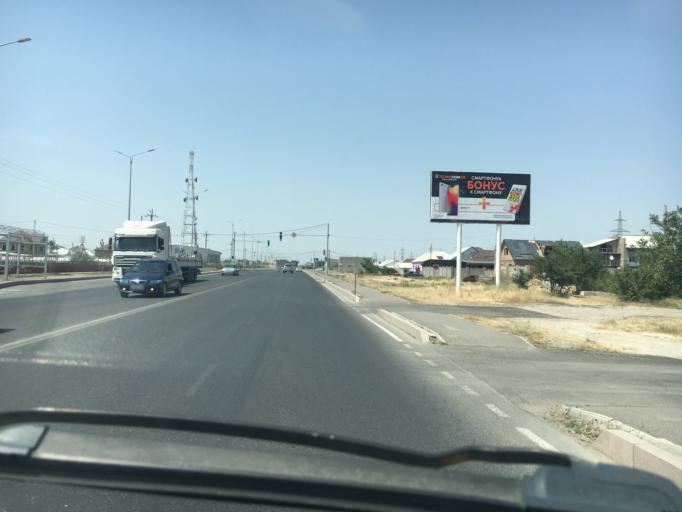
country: KZ
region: Zhambyl
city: Taraz
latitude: 42.8824
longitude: 71.3213
